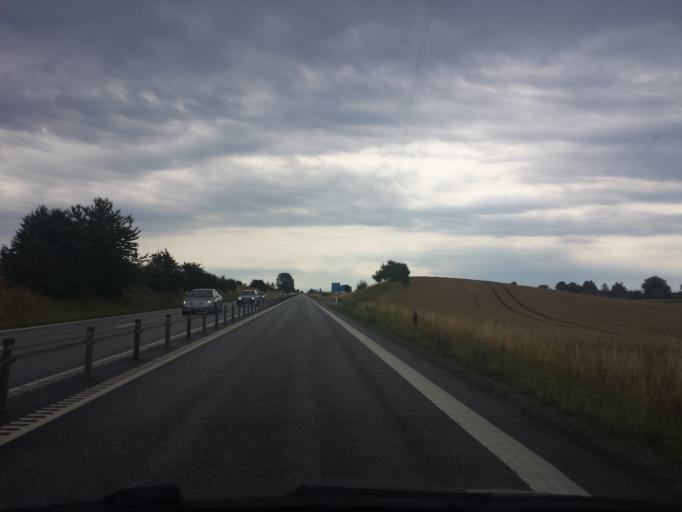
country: SE
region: Skane
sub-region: Ystads Kommun
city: Ystad
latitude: 55.4583
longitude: 13.7359
